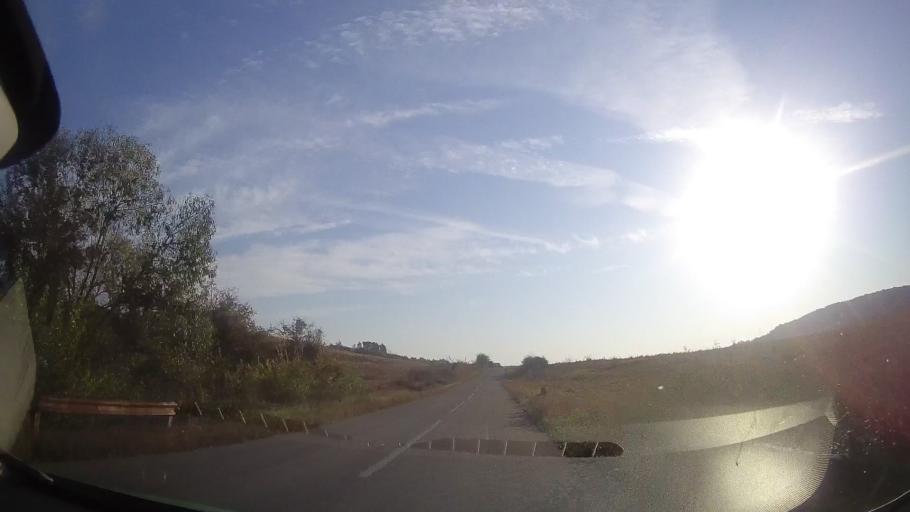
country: RO
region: Timis
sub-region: Comuna Bogda
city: Bogda
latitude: 45.9819
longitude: 21.5416
